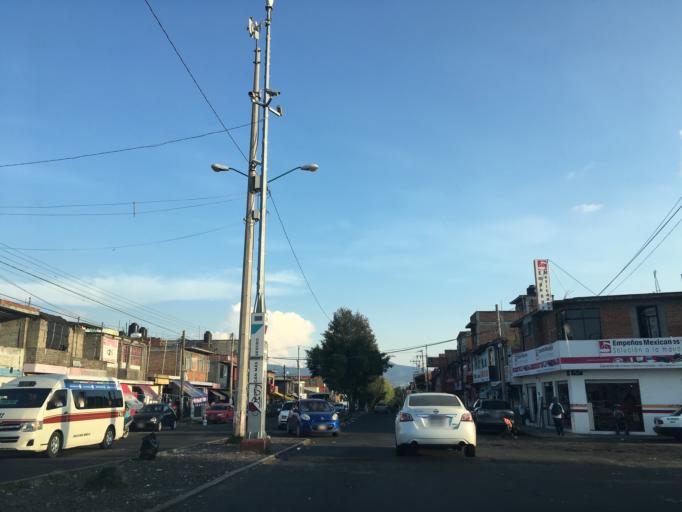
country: MX
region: Michoacan
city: Morelia
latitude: 19.7174
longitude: -101.2163
